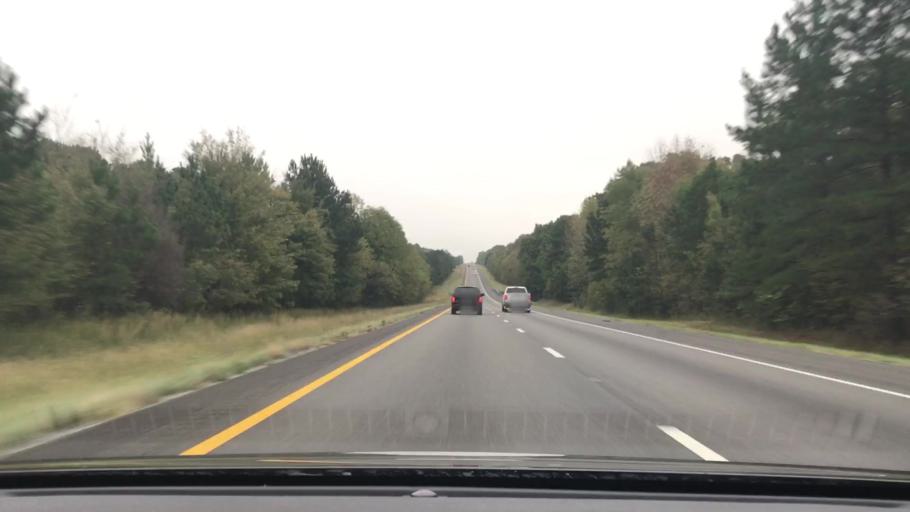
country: US
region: Tennessee
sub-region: Sumner County
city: White House
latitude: 36.4402
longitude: -86.7034
